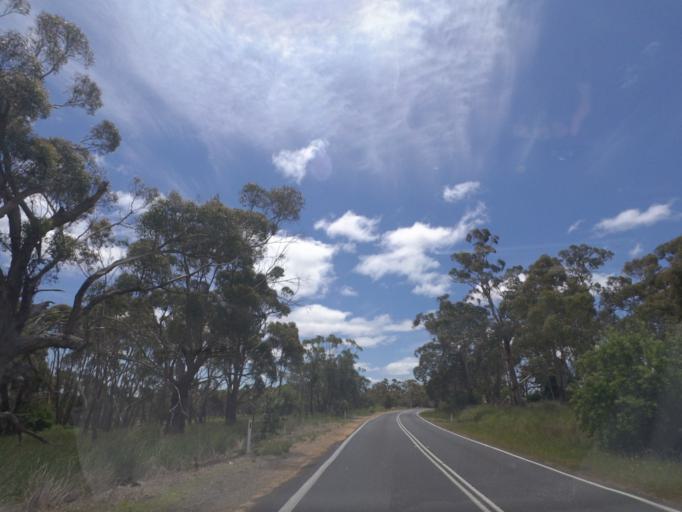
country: AU
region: Victoria
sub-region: Mount Alexander
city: Castlemaine
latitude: -37.3220
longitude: 144.1626
